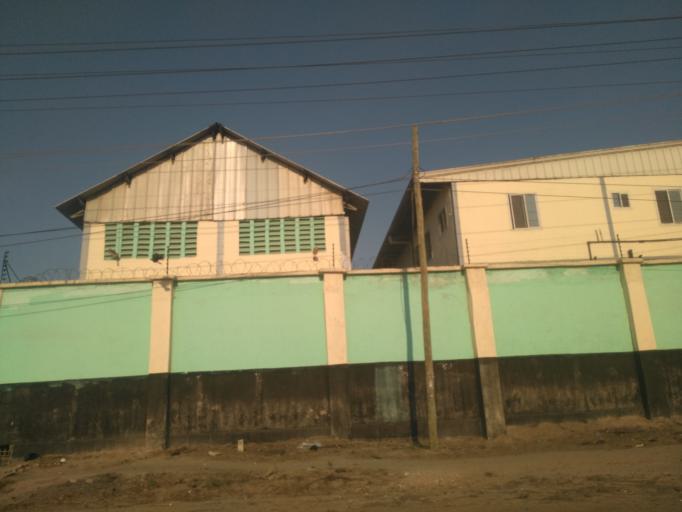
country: TZ
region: Dar es Salaam
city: Dar es Salaam
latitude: -6.9133
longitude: 39.2655
